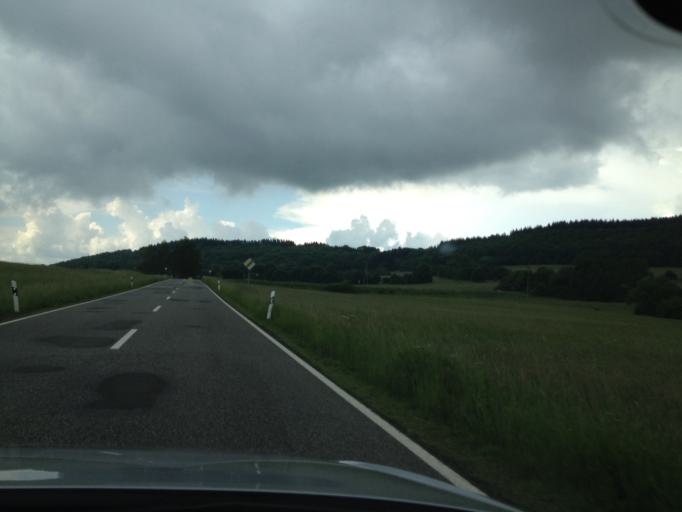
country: DE
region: Saarland
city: Freisen
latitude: 49.5251
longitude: 7.2269
